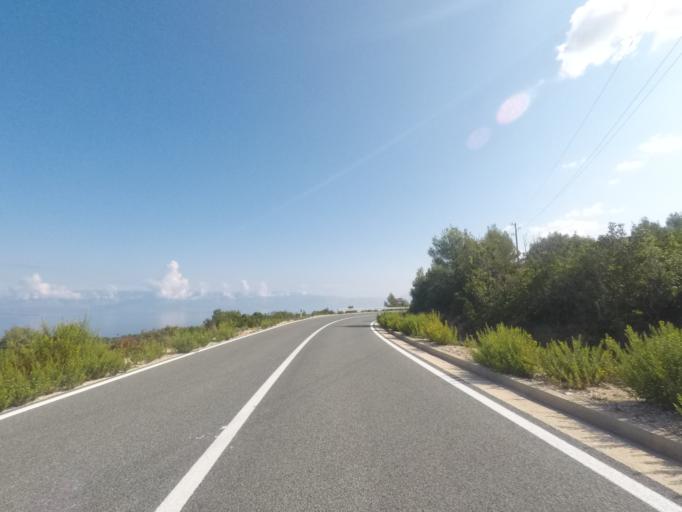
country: HR
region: Splitsko-Dalmatinska
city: Jelsa
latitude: 43.1465
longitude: 16.7733
